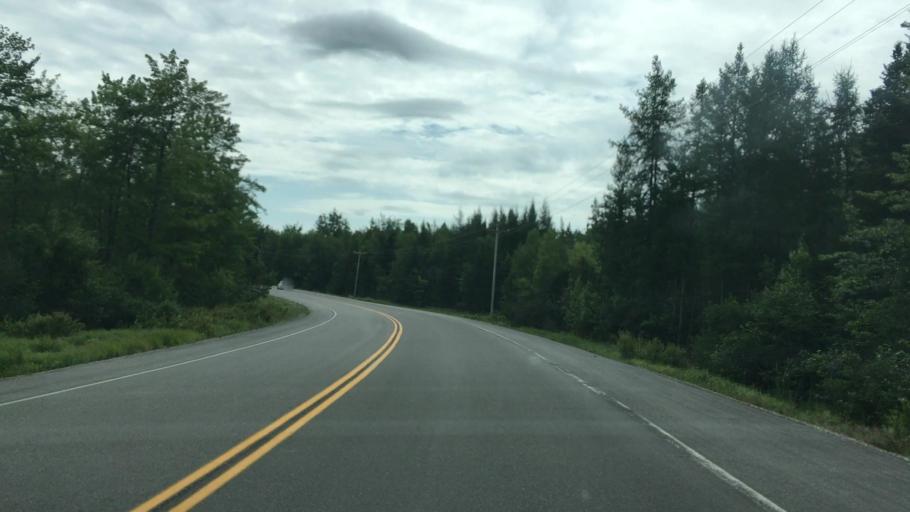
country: US
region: Maine
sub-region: Washington County
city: Machias
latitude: 44.9991
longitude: -67.5686
